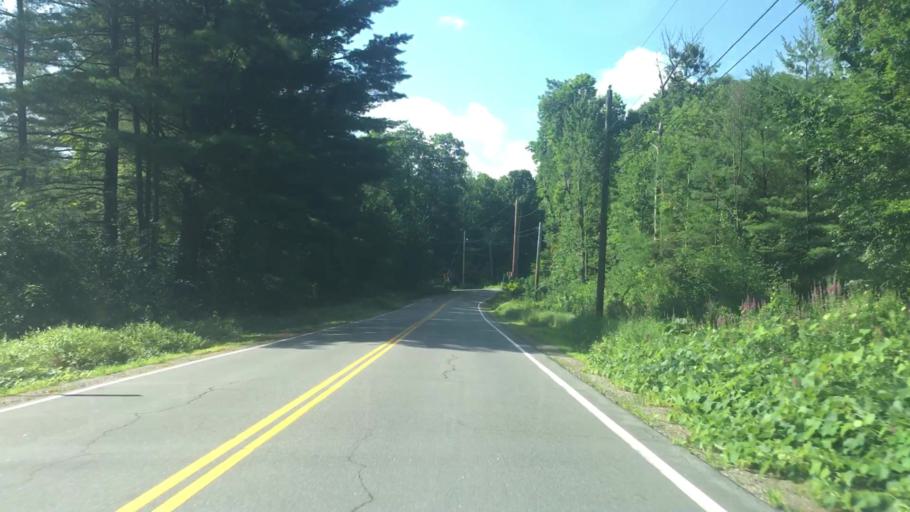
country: US
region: New Hampshire
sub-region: Belknap County
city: Gilford
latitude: 43.5353
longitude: -71.3220
